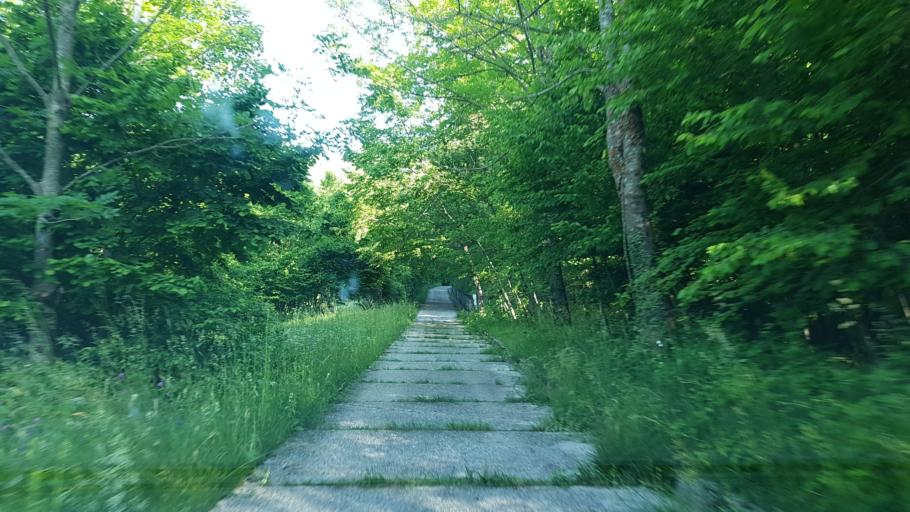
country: IT
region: Friuli Venezia Giulia
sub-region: Provincia di Udine
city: Moggio di Sotto
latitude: 46.4107
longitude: 13.1878
